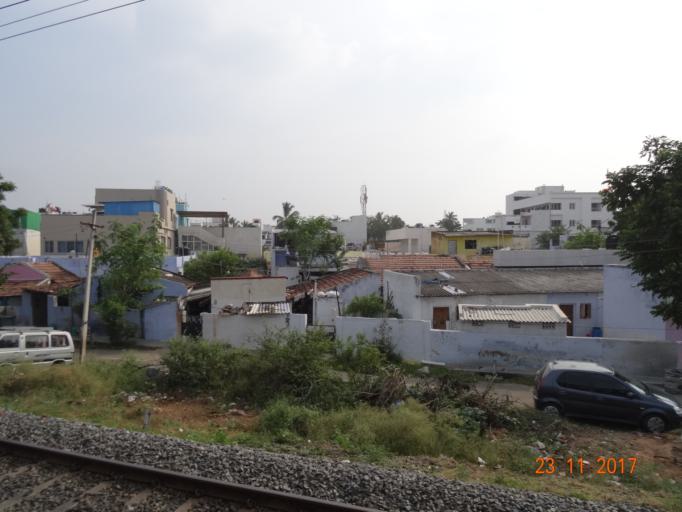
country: IN
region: Tamil Nadu
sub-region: Coimbatore
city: Coimbatore
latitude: 11.0293
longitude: 76.9707
